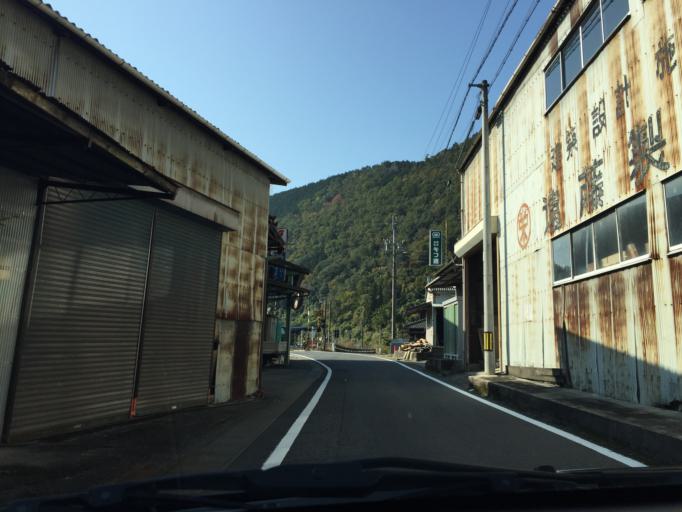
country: JP
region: Gifu
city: Minokamo
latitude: 35.5403
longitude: 137.1153
